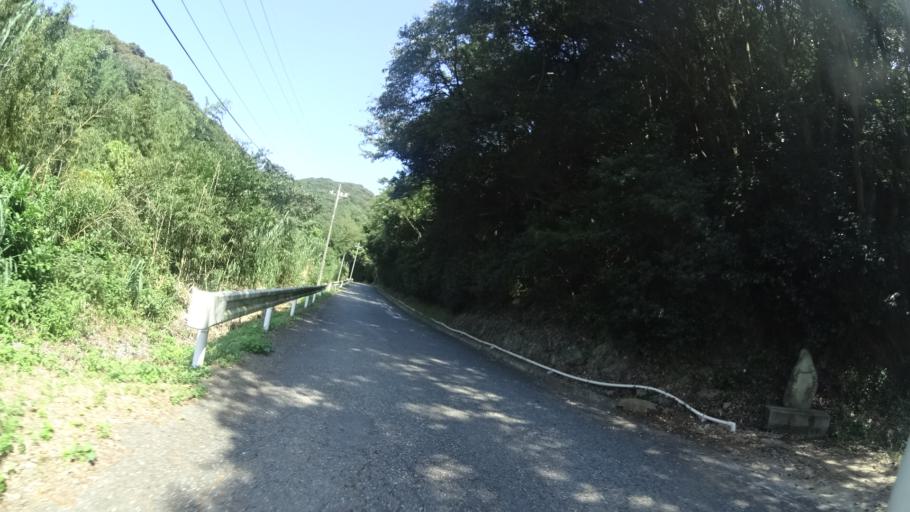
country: JP
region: Yamaguchi
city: Shimonoseki
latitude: 34.1050
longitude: 130.8689
